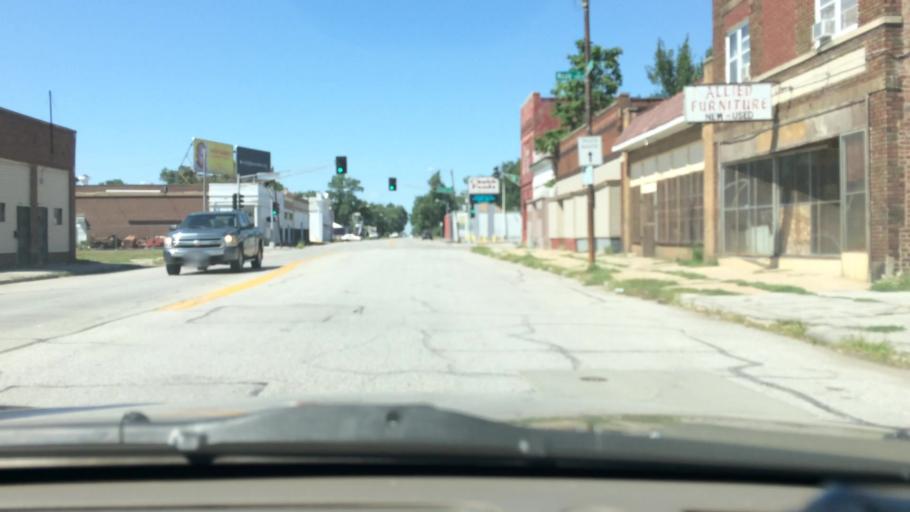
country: US
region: Iowa
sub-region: Pottawattamie County
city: Carter Lake
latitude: 41.2845
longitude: -95.9374
